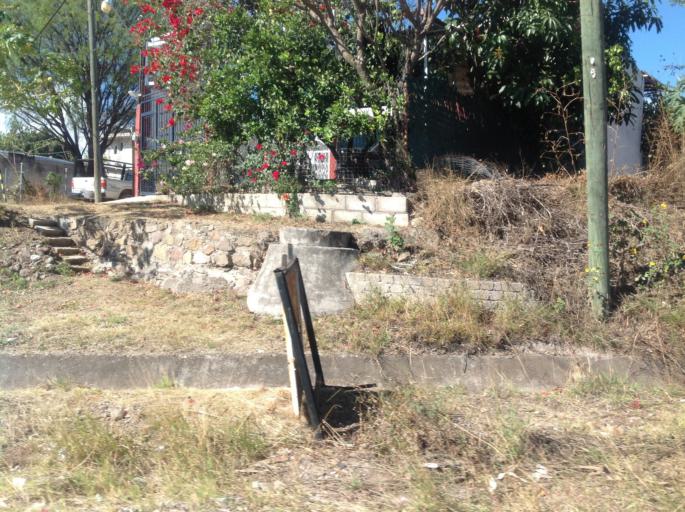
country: MX
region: Oaxaca
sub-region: Heroica Ciudad de Huajuapan de Leon
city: La Junta
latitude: 17.8202
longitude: -97.7609
